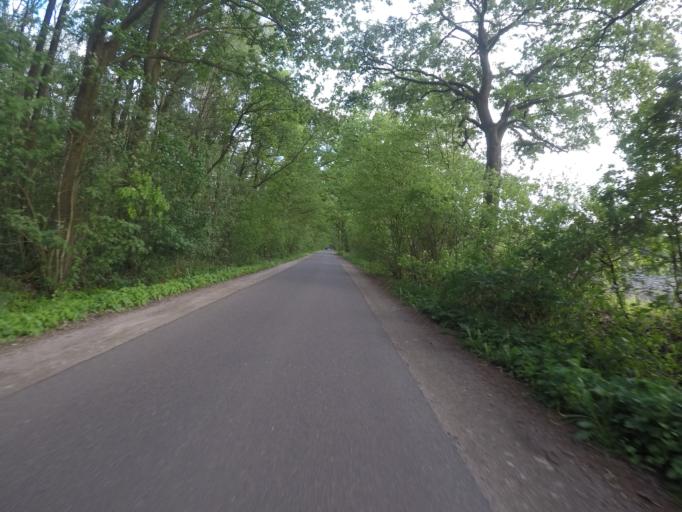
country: DE
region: Schleswig-Holstein
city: Bonningstedt
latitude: 53.6567
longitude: 9.9265
